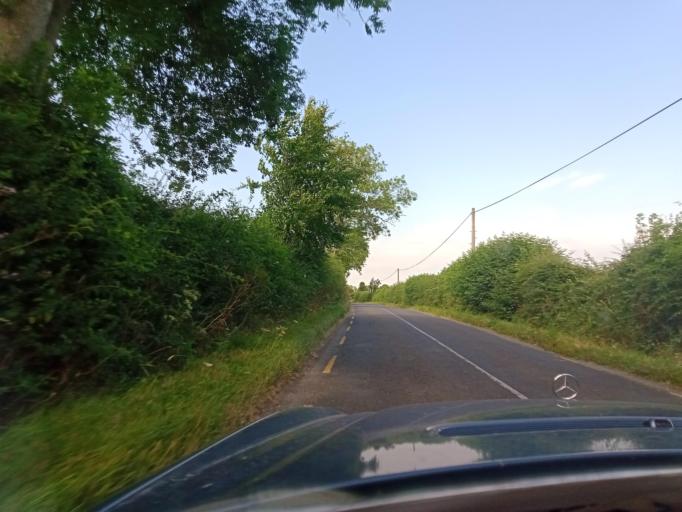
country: IE
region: Leinster
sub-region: Kilkenny
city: Callan
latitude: 52.5184
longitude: -7.3060
